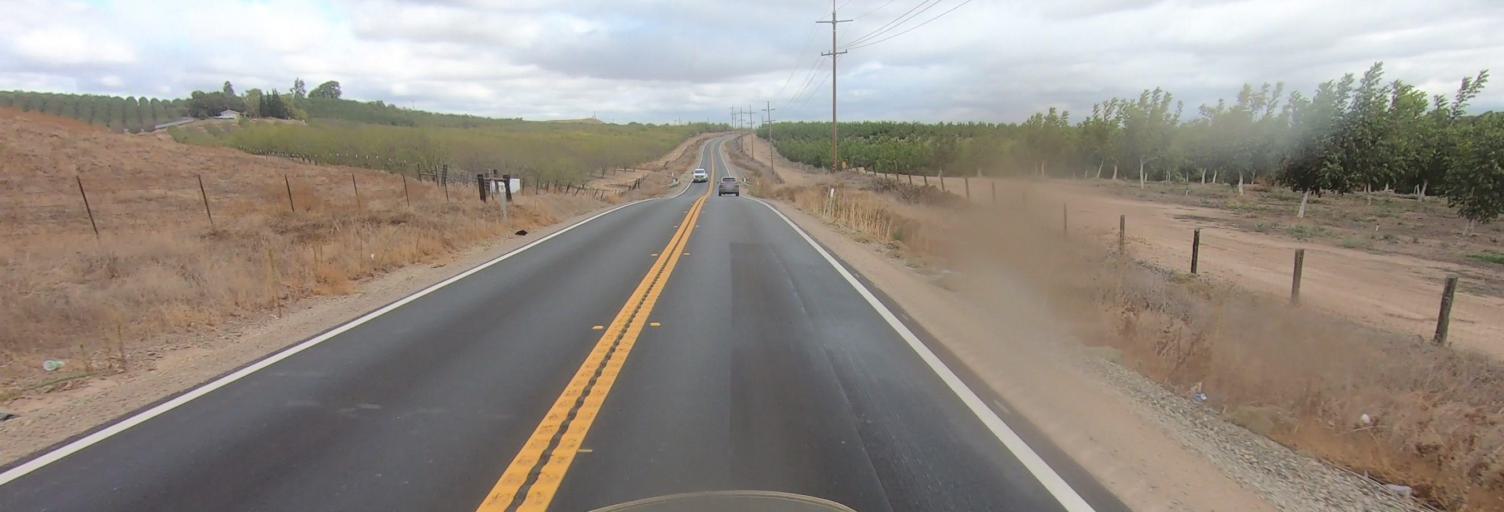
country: US
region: California
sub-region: San Joaquin County
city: Linden
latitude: 38.0642
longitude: -121.0038
